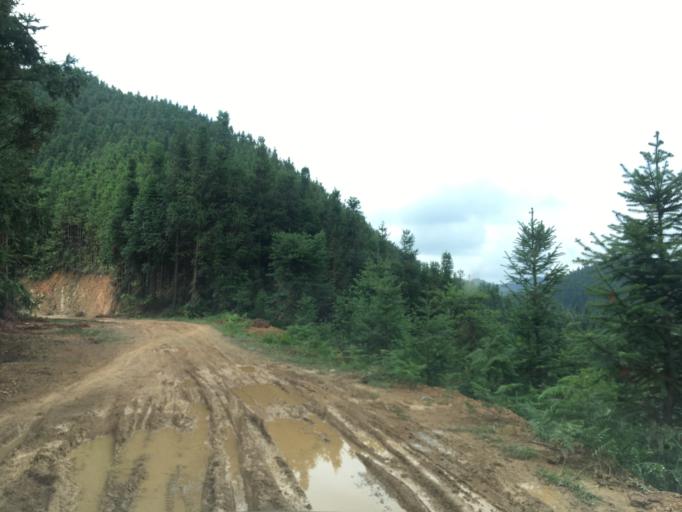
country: CN
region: Guangxi Zhuangzu Zizhiqu
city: Xinzhou
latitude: 24.8685
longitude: 105.8479
